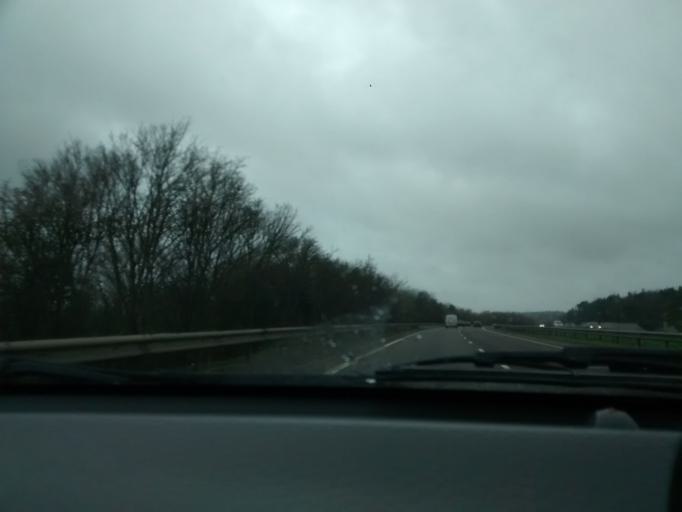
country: GB
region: England
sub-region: Suffolk
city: Bramford
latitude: 52.1046
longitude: 1.1069
